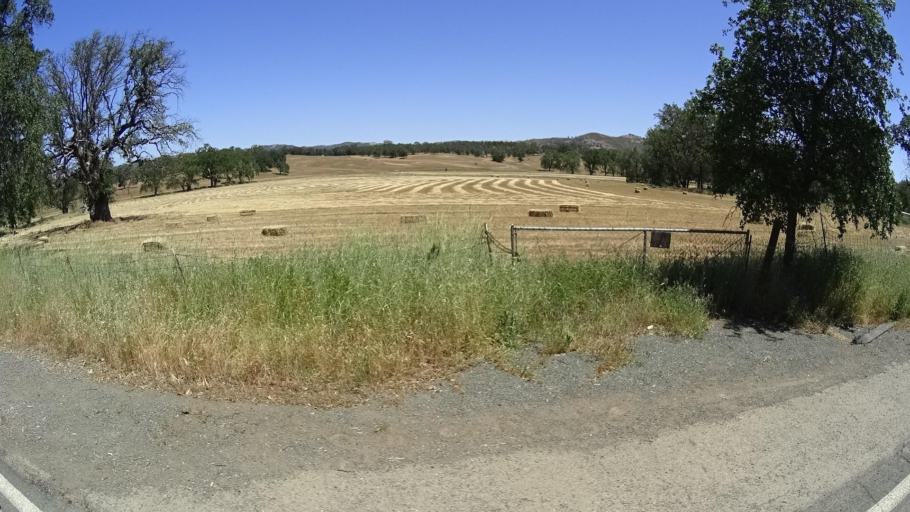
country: US
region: California
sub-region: Lake County
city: Lower Lake
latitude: 38.9087
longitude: -122.6006
